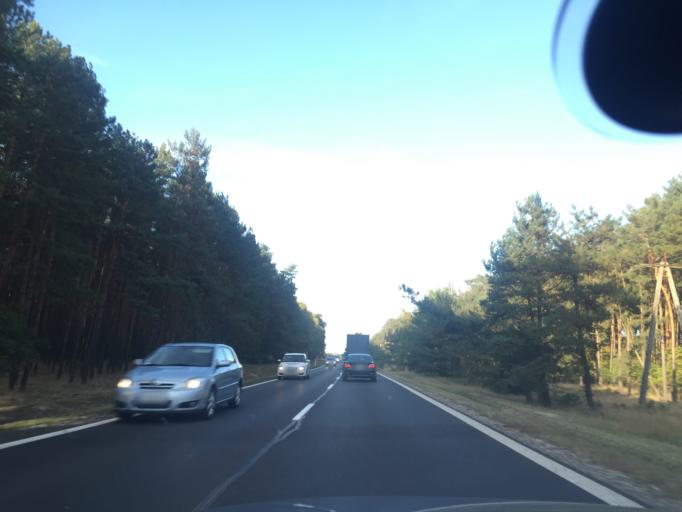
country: PL
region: Kujawsko-Pomorskie
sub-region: Powiat torunski
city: Wielka Nieszawka
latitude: 52.9613
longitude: 18.5358
